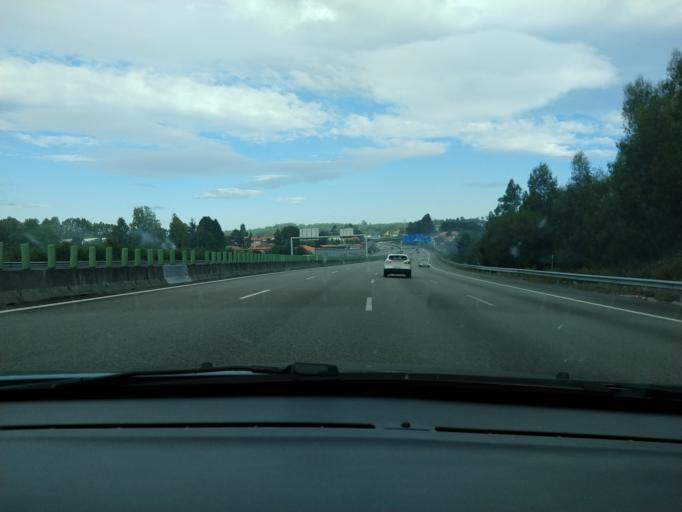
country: PT
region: Porto
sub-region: Vila Nova de Gaia
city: Perozinho
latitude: 41.0570
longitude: -8.5777
